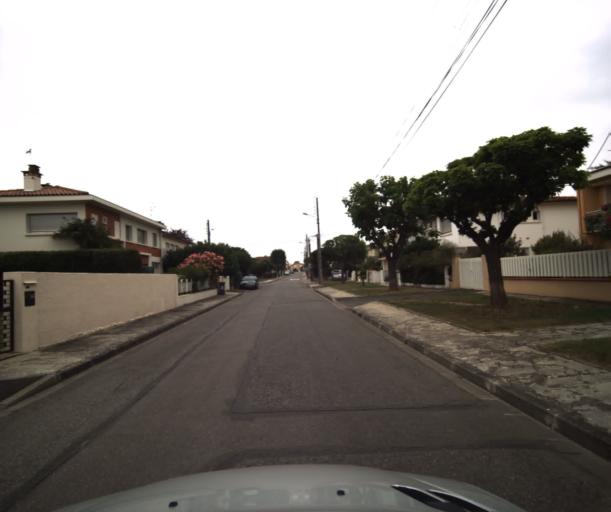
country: FR
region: Midi-Pyrenees
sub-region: Departement de la Haute-Garonne
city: Portet-sur-Garonne
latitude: 43.5180
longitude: 1.4011
